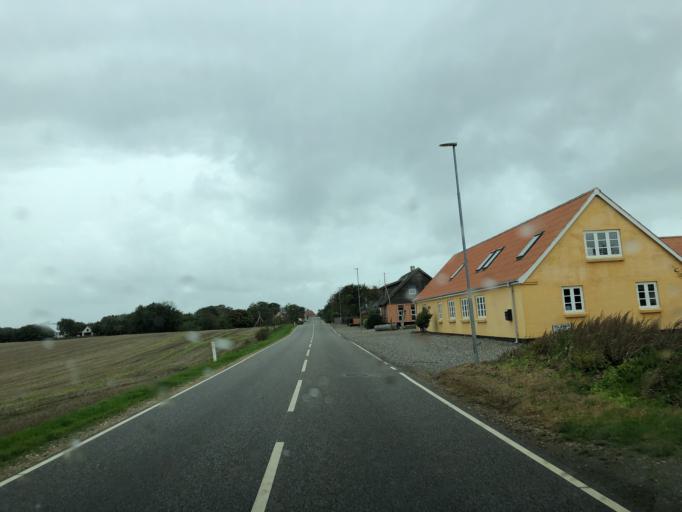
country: DK
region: North Denmark
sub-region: Thisted Kommune
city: Hurup
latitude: 56.7206
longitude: 8.3650
